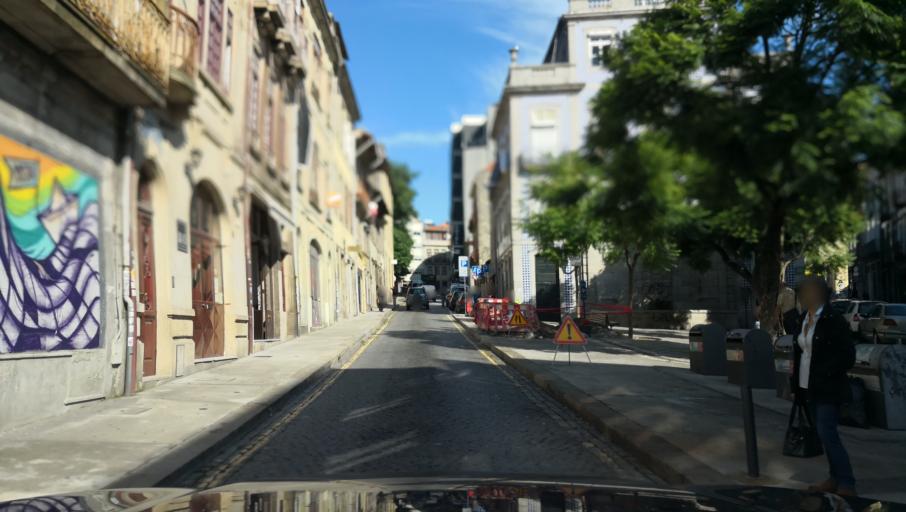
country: PT
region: Porto
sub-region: Porto
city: Porto
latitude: 41.1502
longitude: -8.6148
